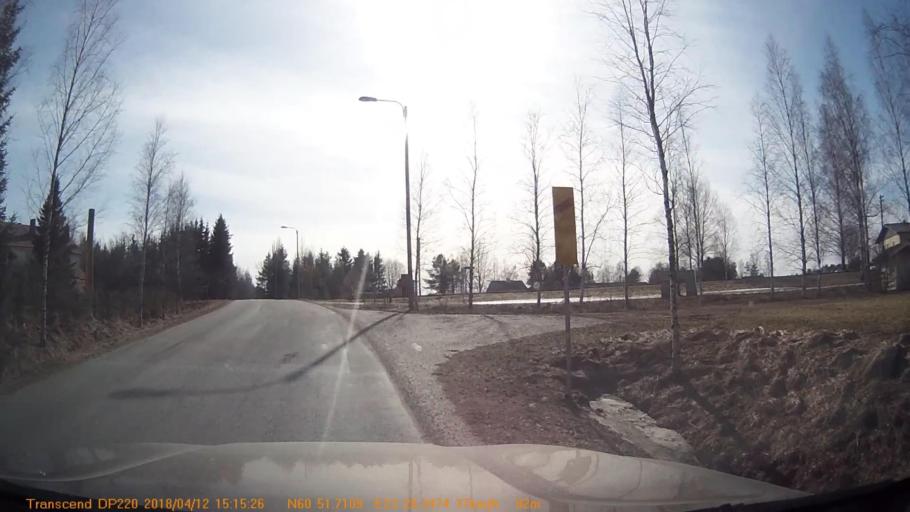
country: FI
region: Haeme
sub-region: Forssa
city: Jokioinen
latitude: 60.8618
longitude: 23.4390
